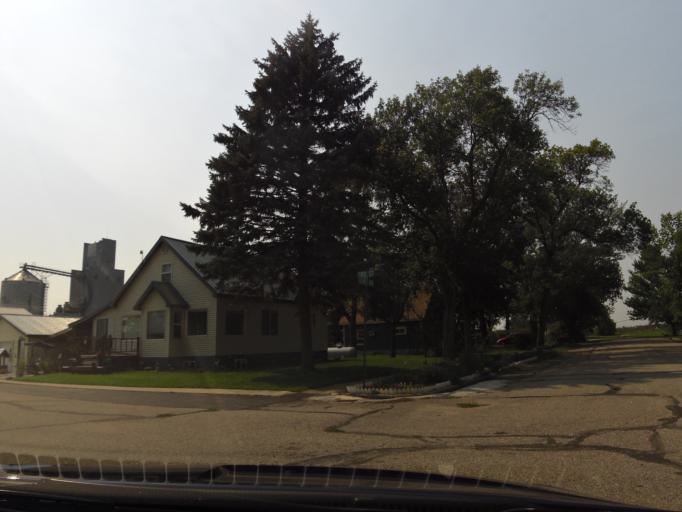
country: US
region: South Dakota
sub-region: Roberts County
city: Sisseton
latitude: 45.8568
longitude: -97.1058
